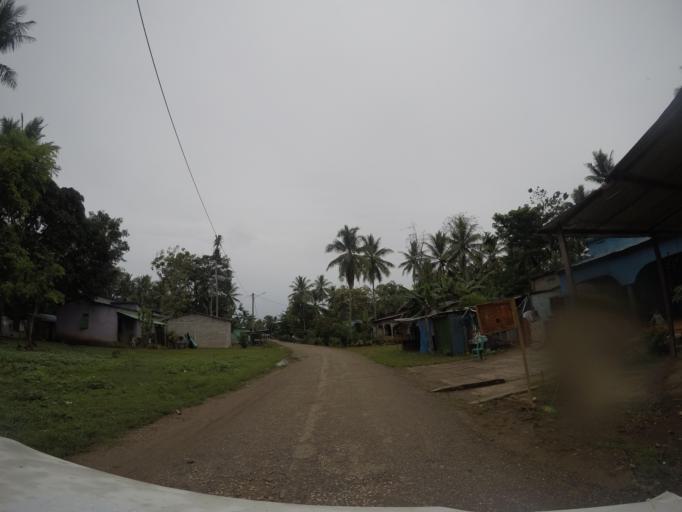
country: TL
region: Lautem
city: Lospalos
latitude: -8.5245
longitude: 126.9994
